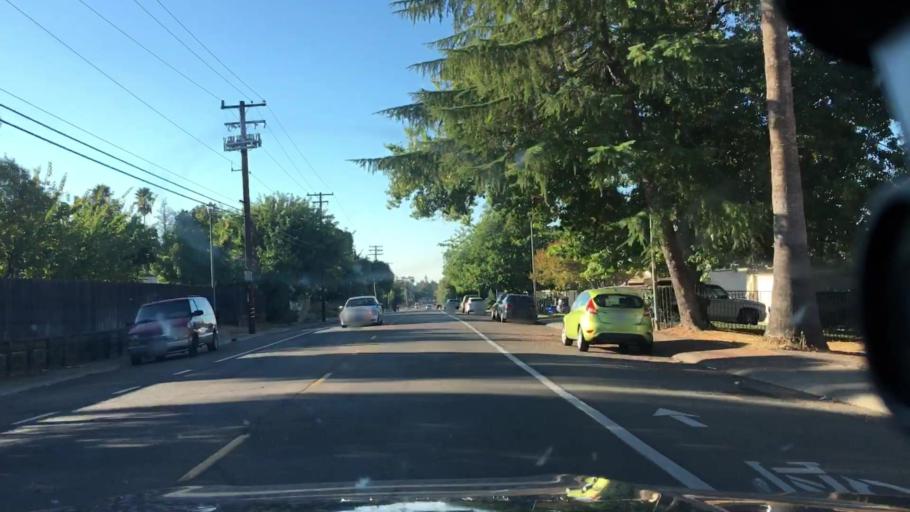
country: US
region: California
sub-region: Sacramento County
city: Antelope
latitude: 38.6951
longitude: -121.3366
